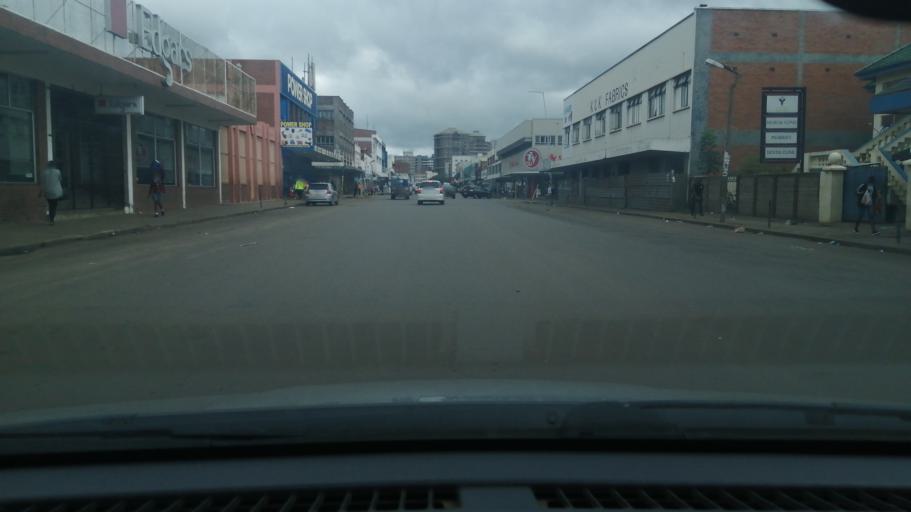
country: ZW
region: Harare
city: Harare
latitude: -17.8372
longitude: 31.0441
